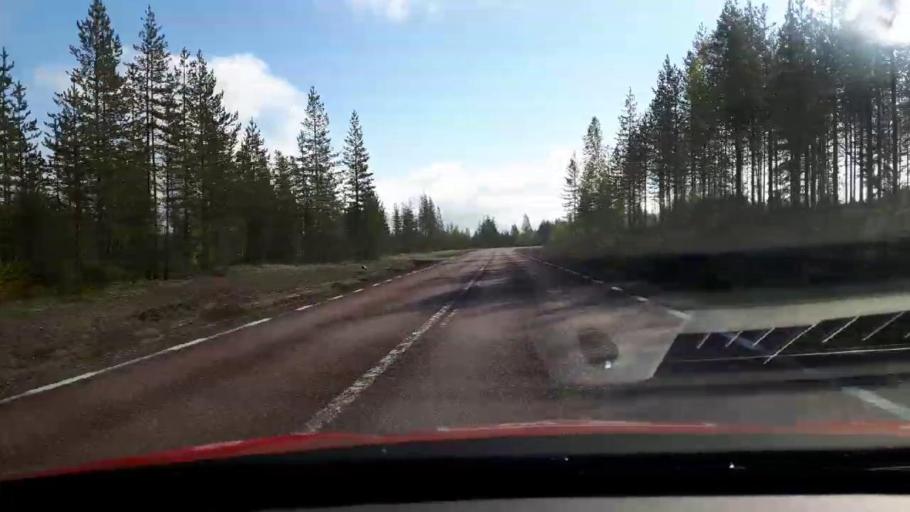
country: SE
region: Gaevleborg
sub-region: Ljusdals Kommun
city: Farila
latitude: 61.9008
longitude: 15.6437
